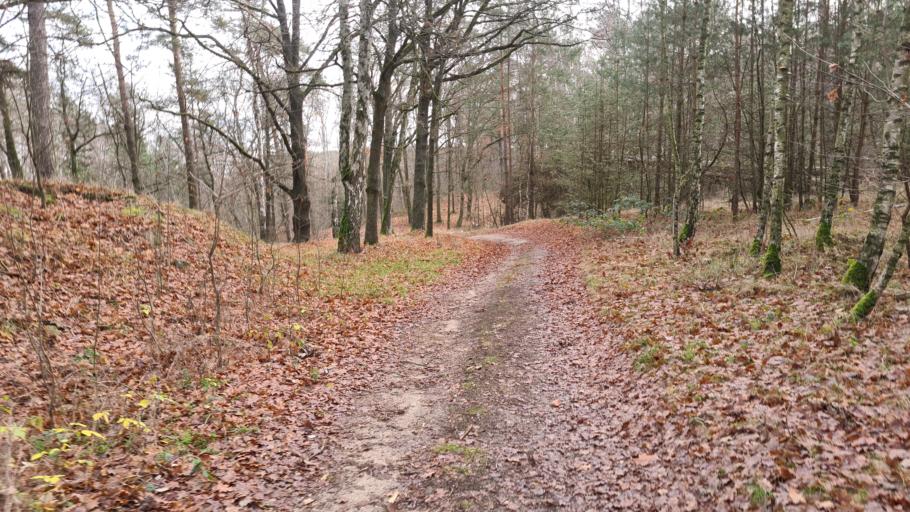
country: DE
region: Brandenburg
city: Groden
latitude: 51.3954
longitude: 13.5730
